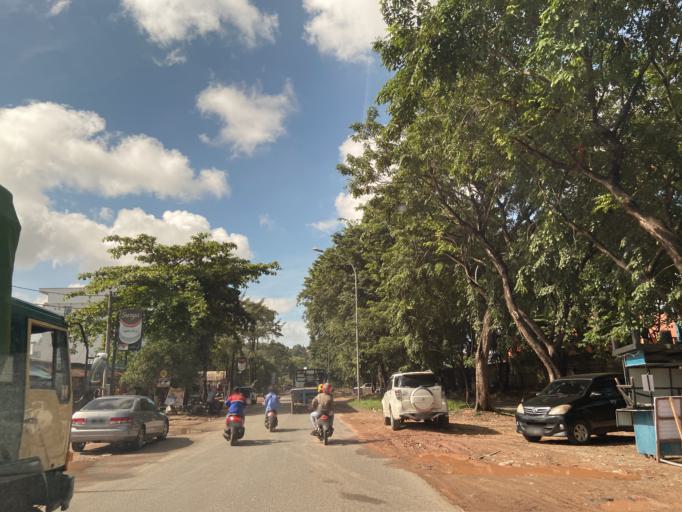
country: SG
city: Singapore
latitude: 1.1653
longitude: 104.0119
